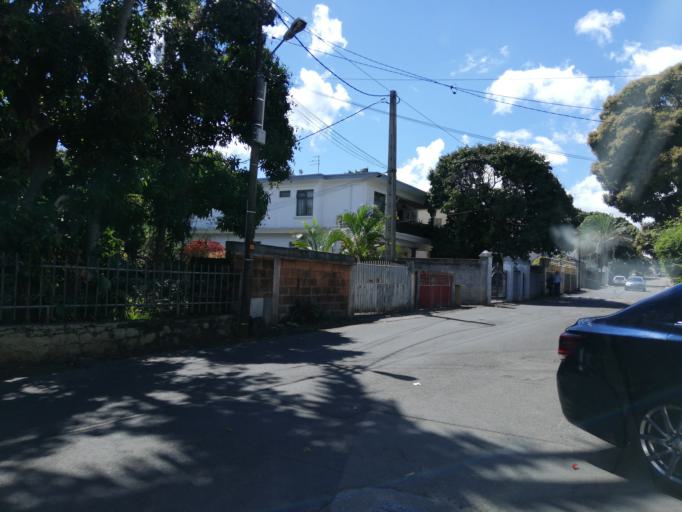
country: MU
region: Moka
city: Moka
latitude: -20.2258
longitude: 57.4648
